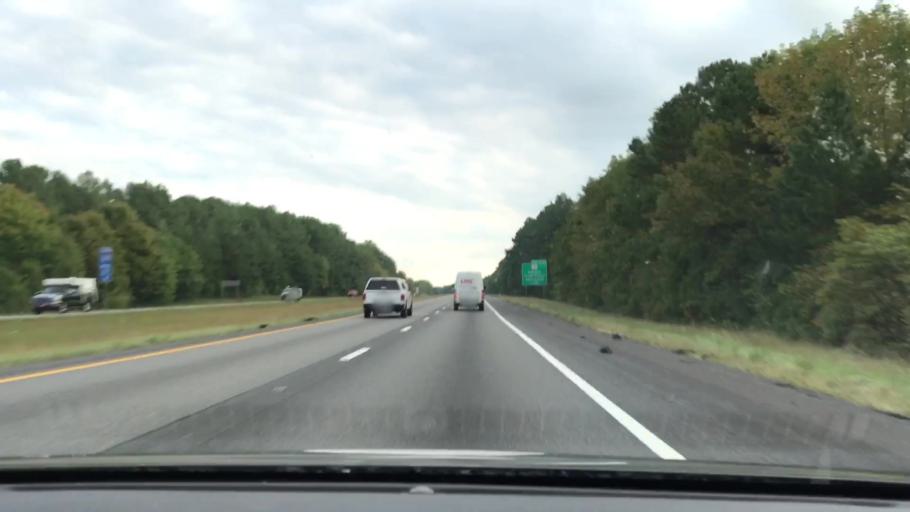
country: US
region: Tennessee
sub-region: Sumner County
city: White House
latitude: 36.5121
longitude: -86.6542
